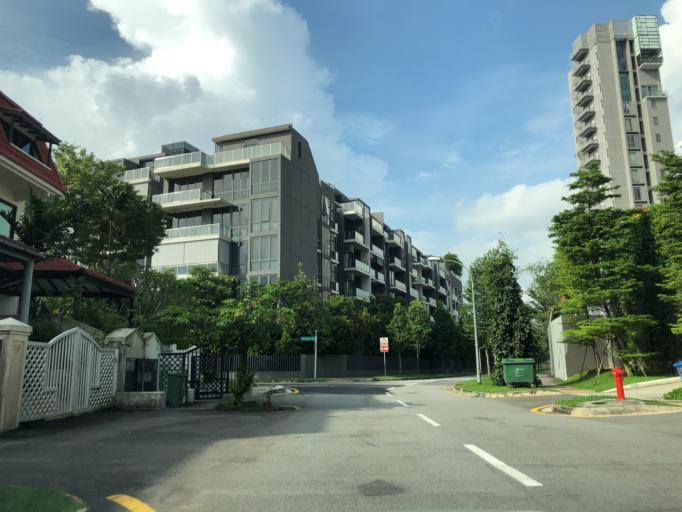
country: SG
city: Singapore
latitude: 1.3177
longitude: 103.8282
